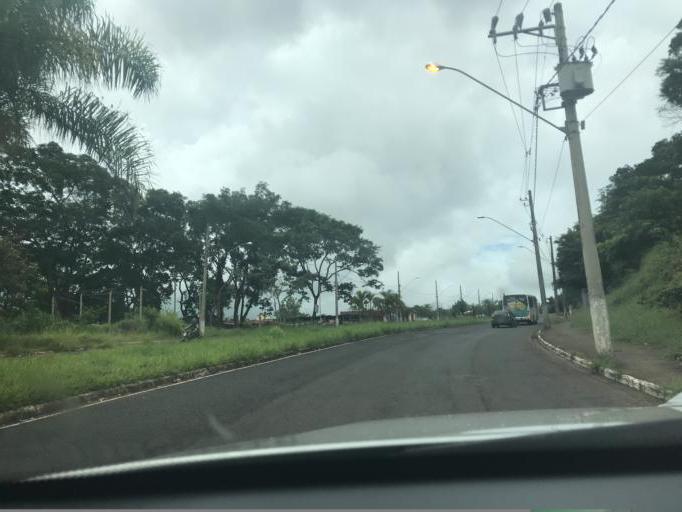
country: BR
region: Minas Gerais
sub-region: Araxa
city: Araxa
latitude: -19.5811
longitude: -46.9416
